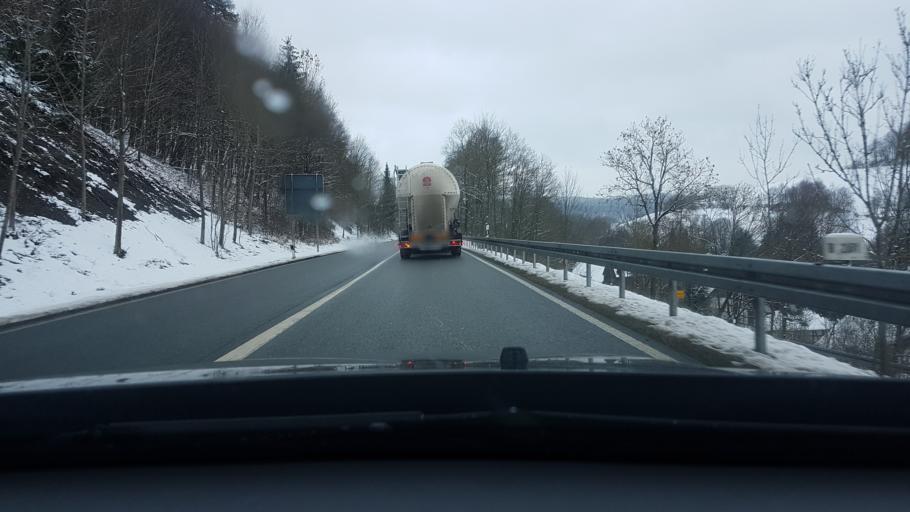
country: DE
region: North Rhine-Westphalia
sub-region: Regierungsbezirk Arnsberg
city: Medebach
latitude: 51.2860
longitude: 8.7568
